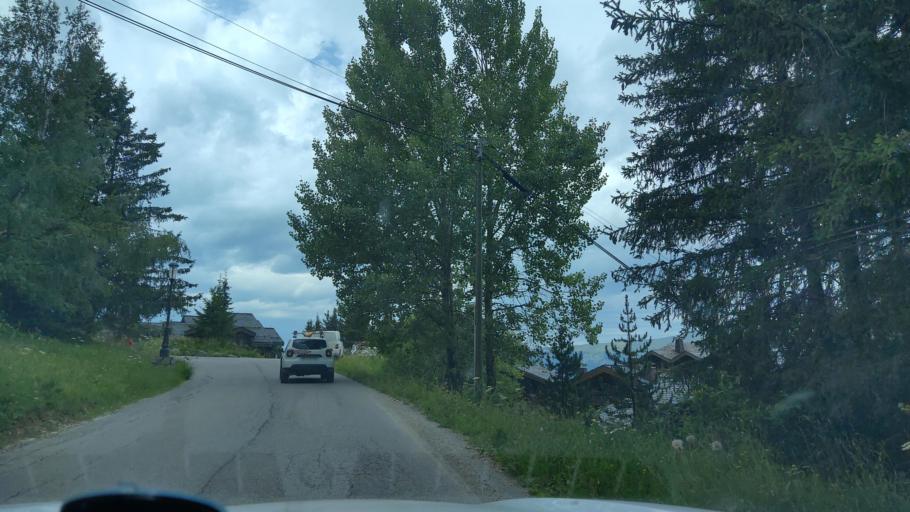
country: FR
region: Rhone-Alpes
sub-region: Departement de la Savoie
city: Courchevel
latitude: 45.4110
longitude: 6.6586
